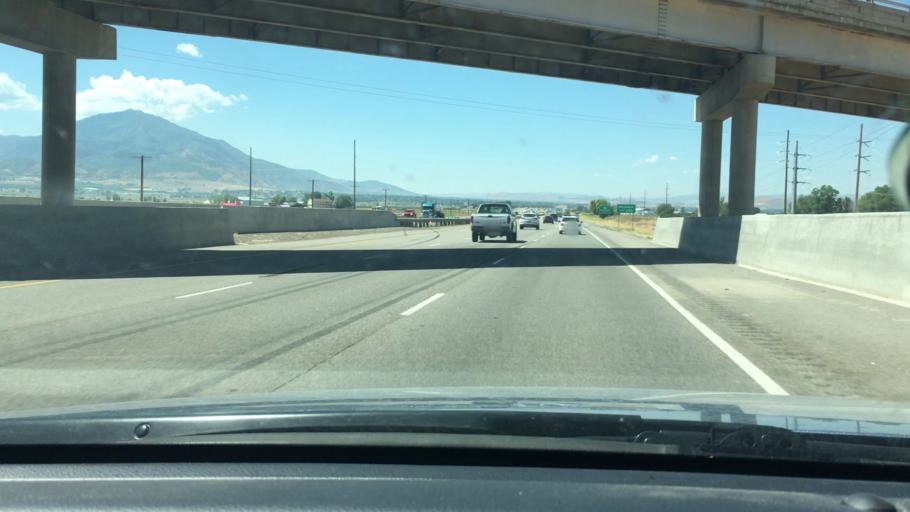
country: US
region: Utah
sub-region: Utah County
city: Spanish Fork
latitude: 40.0975
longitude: -111.6908
